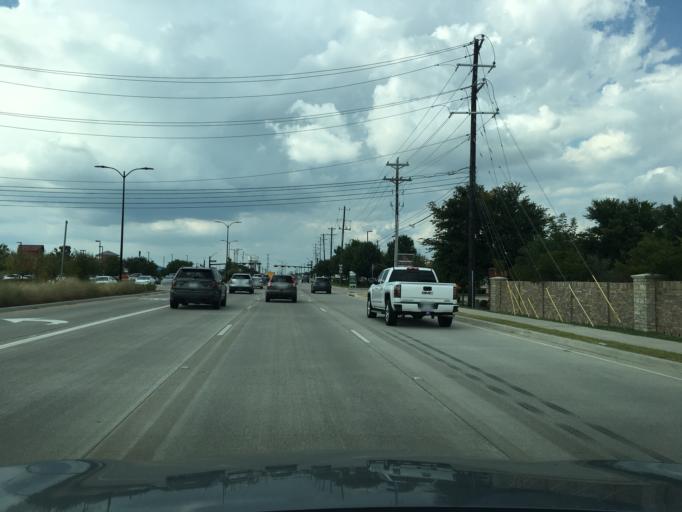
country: US
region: Texas
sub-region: Denton County
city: Little Elm
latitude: 33.1758
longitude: -96.8873
